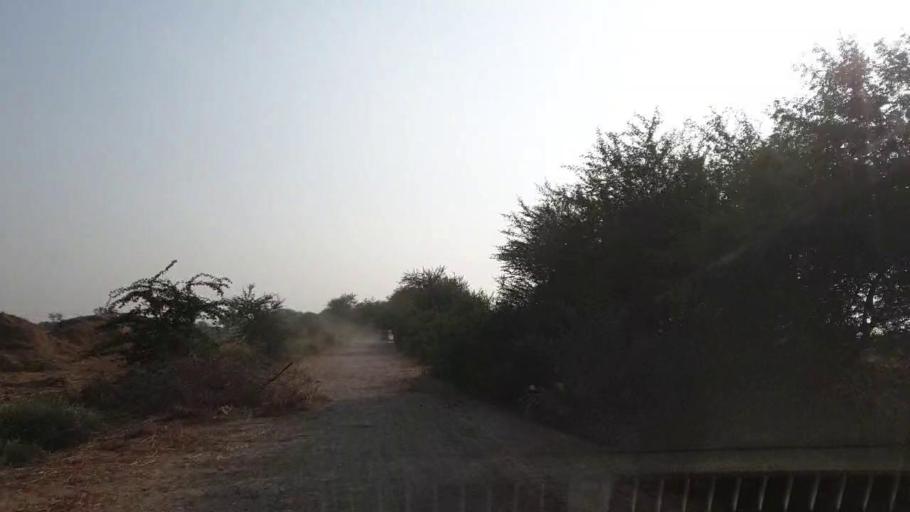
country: PK
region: Sindh
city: Kario
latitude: 24.9011
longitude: 68.5677
